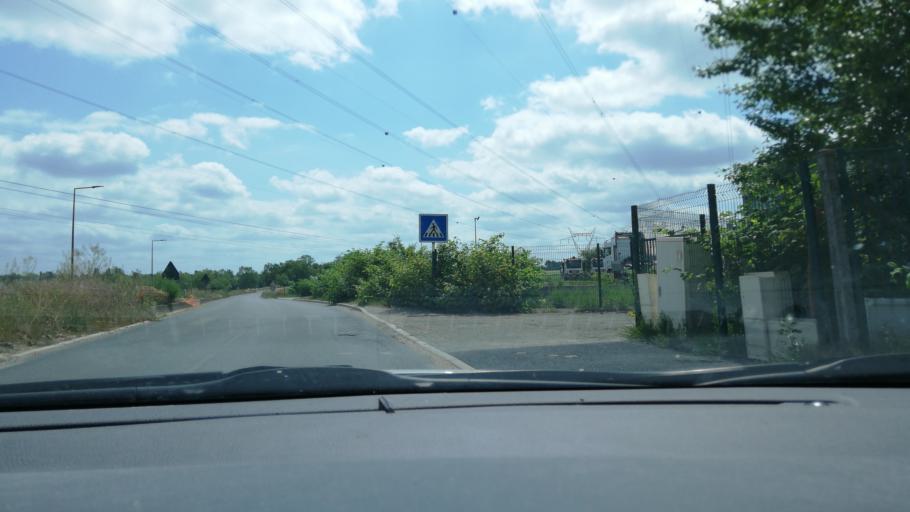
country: FR
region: Ile-de-France
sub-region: Departement du Val-d'Oise
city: Vaureal
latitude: 49.0648
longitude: 2.0215
